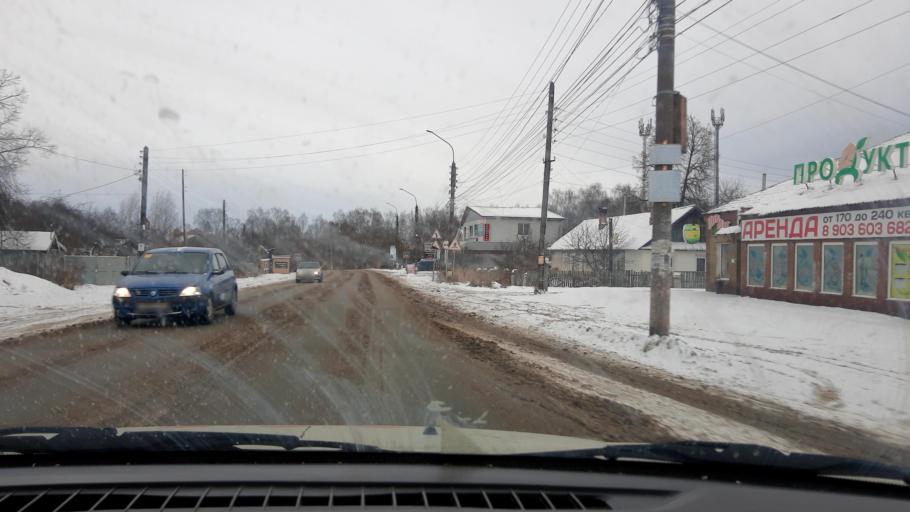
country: RU
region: Nizjnij Novgorod
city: Gorodets
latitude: 56.6569
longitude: 43.4852
